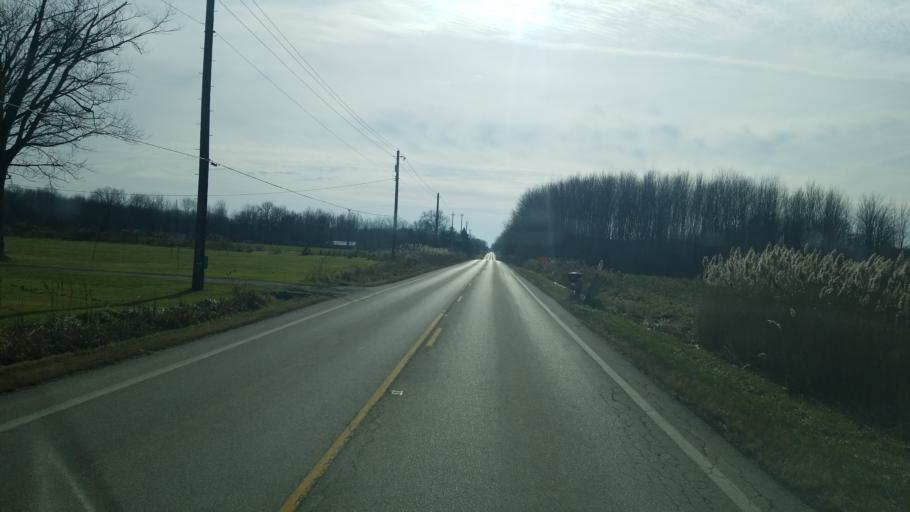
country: US
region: Ohio
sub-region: Ashtabula County
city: Geneva
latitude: 41.7140
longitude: -80.9527
